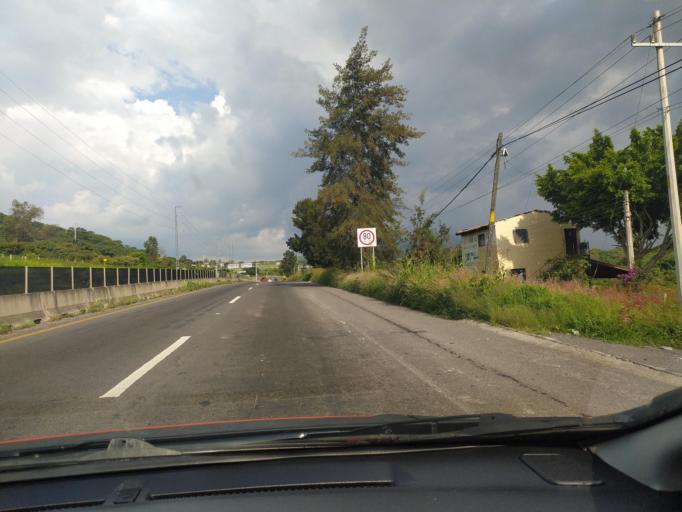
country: MX
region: Jalisco
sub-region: Acatlan de Juarez
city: Villa de los Ninos
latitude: 20.4346
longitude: -103.5754
